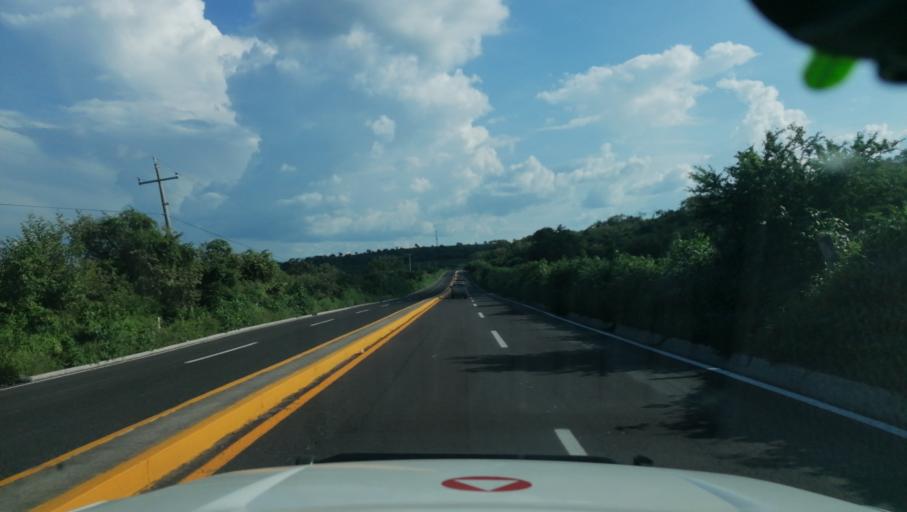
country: MX
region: Morelos
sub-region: Ayala
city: Abelardo L. Rodriguez
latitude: 18.7076
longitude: -98.9910
